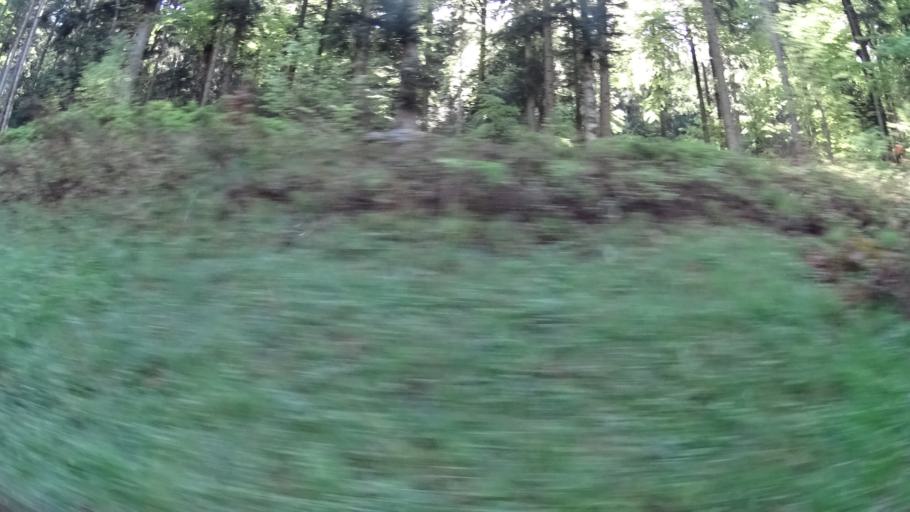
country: DE
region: Baden-Wuerttemberg
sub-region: Karlsruhe Region
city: Bad Wildbad
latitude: 48.7414
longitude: 8.5792
